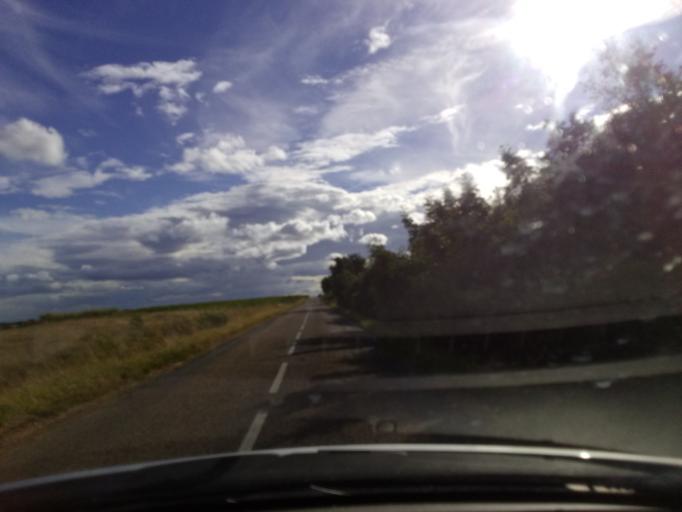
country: FR
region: Languedoc-Roussillon
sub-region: Departement de l'Herault
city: Saint-Jean-de-Fos
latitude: 43.6772
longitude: 3.5321
